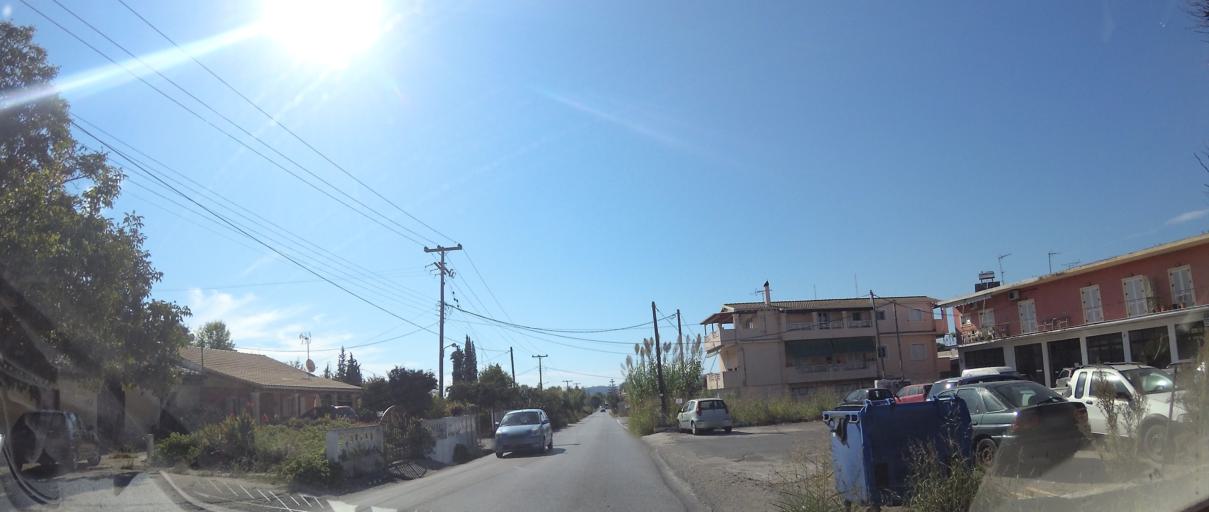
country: GR
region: Ionian Islands
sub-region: Nomos Kerkyras
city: Alepou
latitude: 39.6140
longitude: 19.9035
